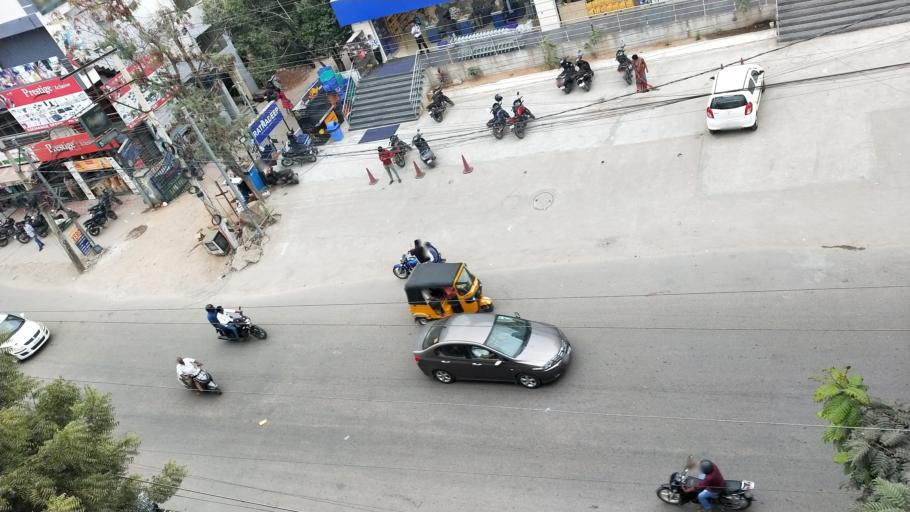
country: IN
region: Telangana
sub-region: Rangareddi
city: Kukatpalli
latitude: 17.4937
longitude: 78.4044
